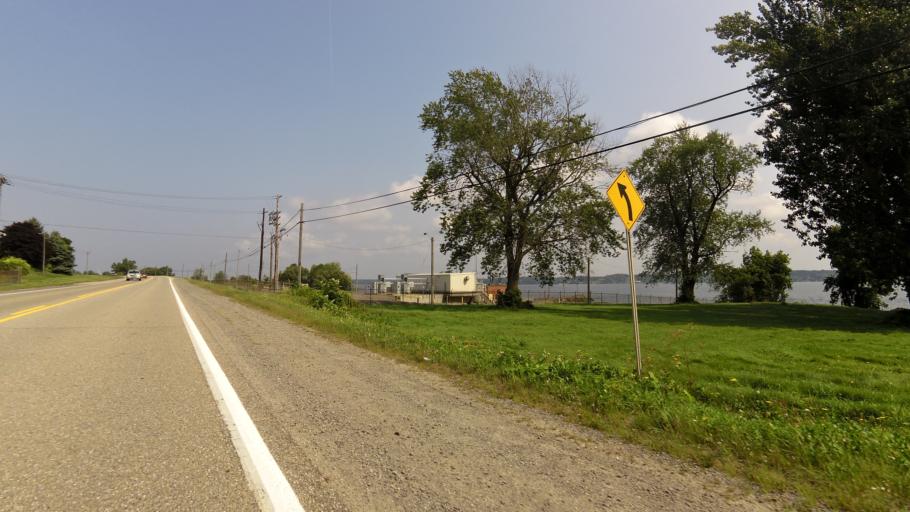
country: CA
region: Ontario
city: Prescott
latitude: 44.6582
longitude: -75.5810
